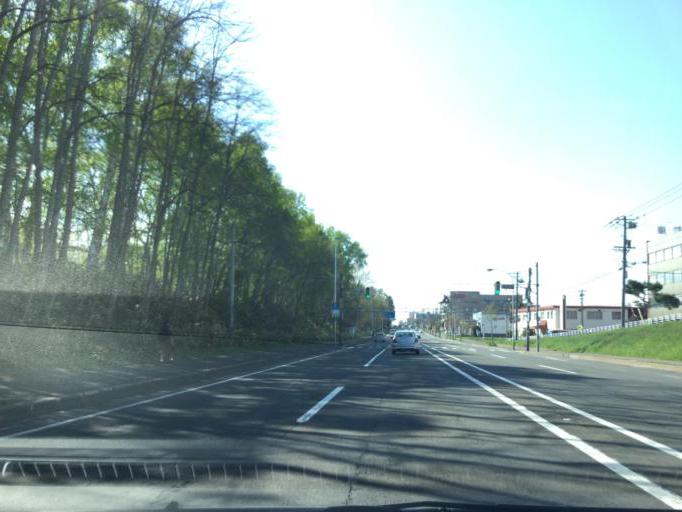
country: JP
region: Hokkaido
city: Sapporo
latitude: 43.0086
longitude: 141.4256
